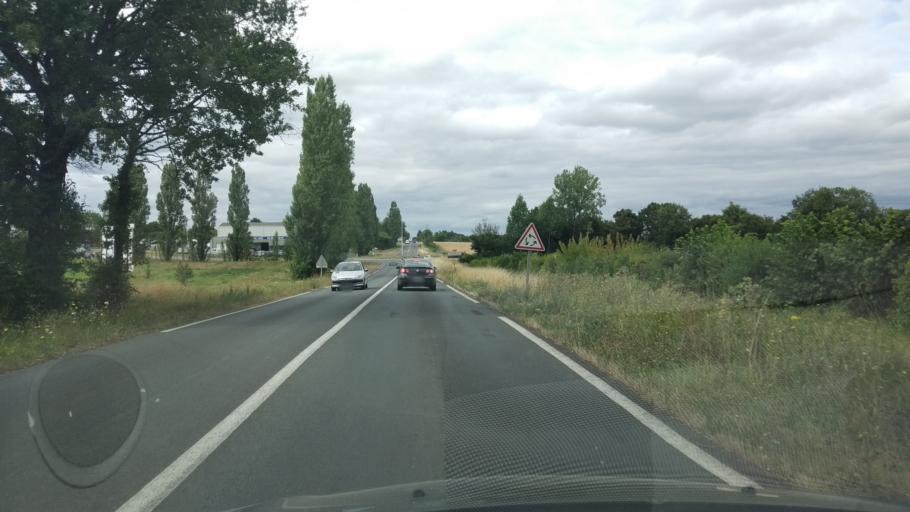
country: FR
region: Poitou-Charentes
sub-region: Departement de la Vienne
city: Smarves
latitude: 46.5038
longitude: 0.3625
